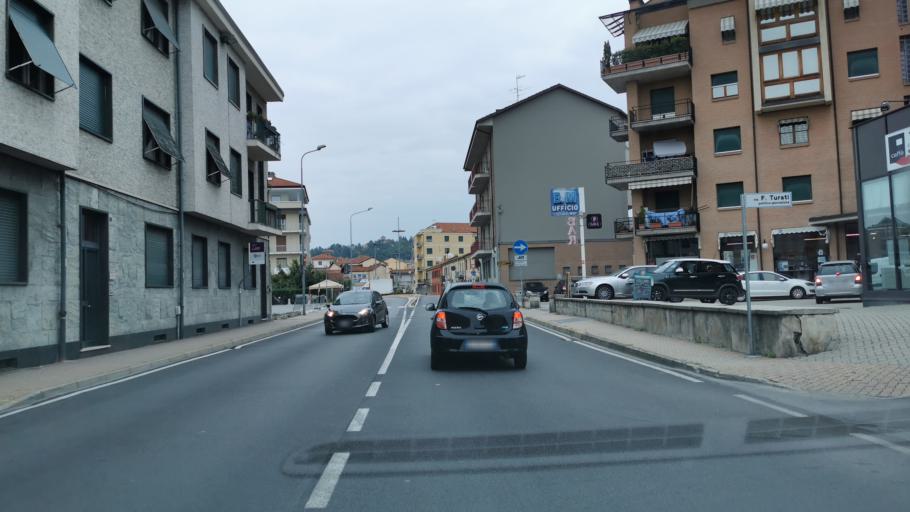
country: IT
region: Piedmont
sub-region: Provincia di Cuneo
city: Bra
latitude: 44.6914
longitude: 7.8549
